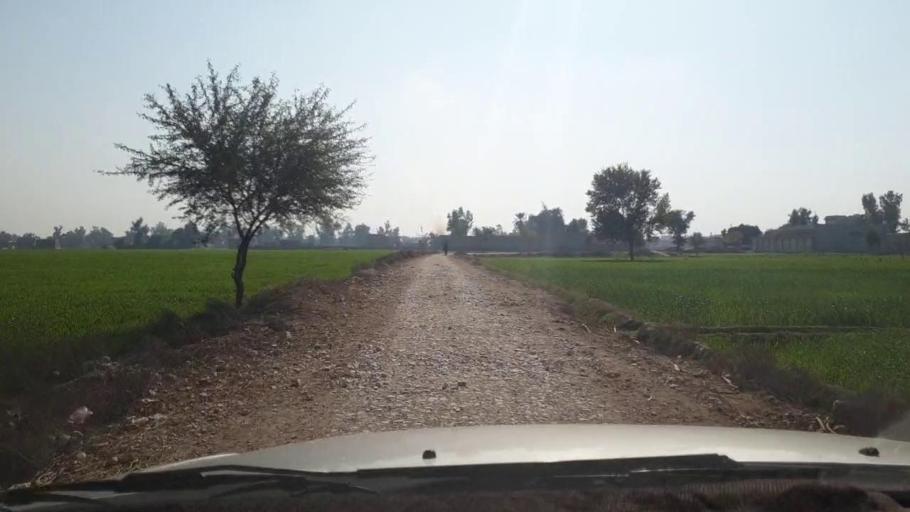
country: PK
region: Sindh
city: Mirpur Mathelo
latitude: 28.0346
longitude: 69.5518
